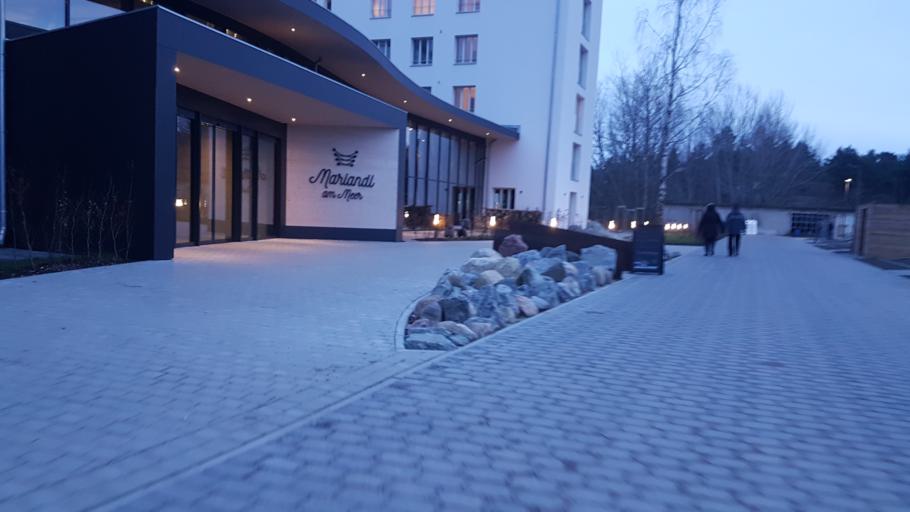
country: DE
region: Mecklenburg-Vorpommern
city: Ostseebad Binz
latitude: 54.4437
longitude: 13.5725
